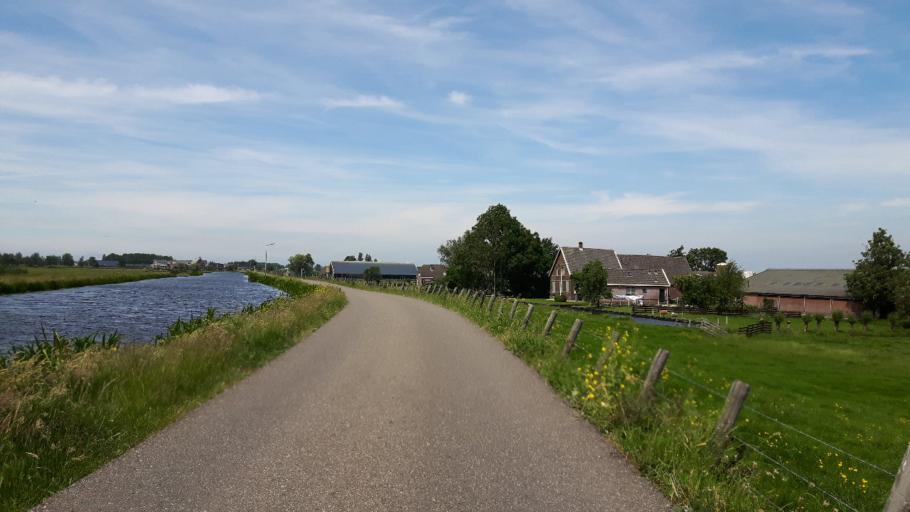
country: NL
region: South Holland
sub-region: Gemeente Nieuwkoop
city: Nieuwkoop
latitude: 52.1513
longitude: 4.7276
